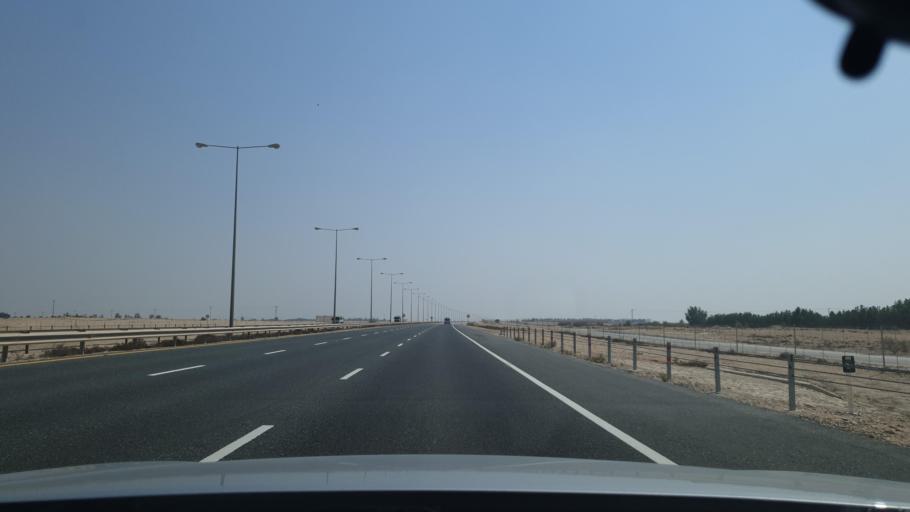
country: QA
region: Al Khawr
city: Al Khawr
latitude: 25.7786
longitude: 51.4059
